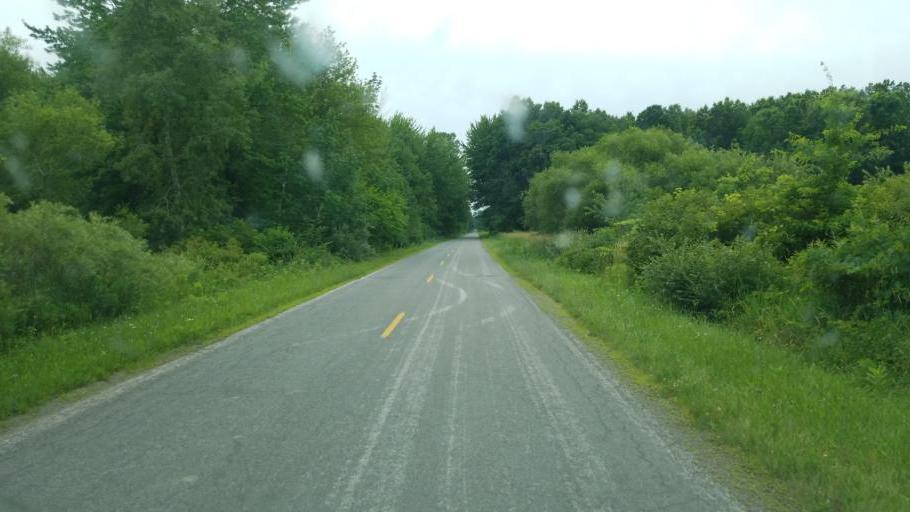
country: US
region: Ohio
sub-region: Trumbull County
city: Cortland
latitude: 41.4246
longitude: -80.7769
